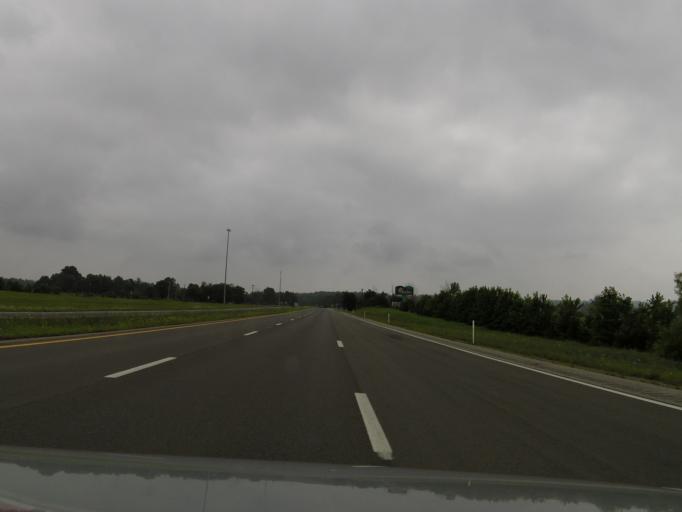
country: US
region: Kentucky
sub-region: Muhlenberg County
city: Greenville
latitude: 37.2356
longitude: -87.2675
